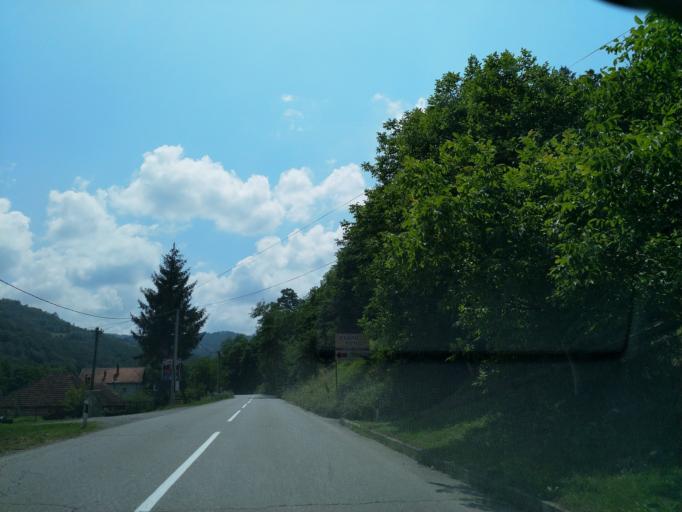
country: RS
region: Central Serbia
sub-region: Rasinski Okrug
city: Aleksandrovac
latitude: 43.3521
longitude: 20.9875
